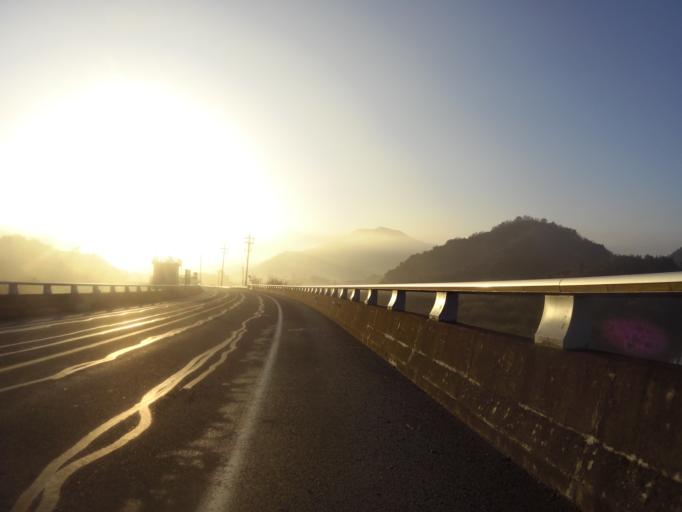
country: KR
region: Gyeongsangnam-do
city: Naeso
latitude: 35.3817
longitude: 128.5219
